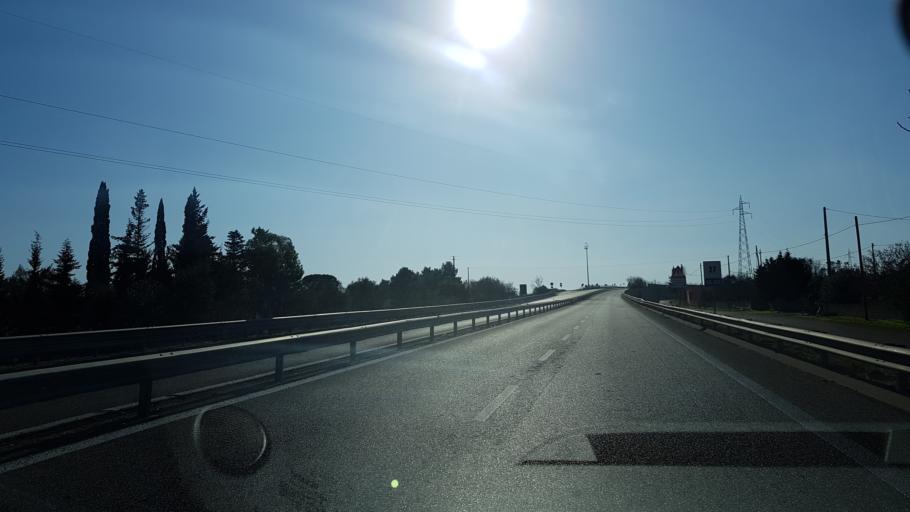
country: IT
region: Apulia
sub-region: Provincia di Lecce
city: Galatone
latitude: 40.1329
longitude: 18.0523
